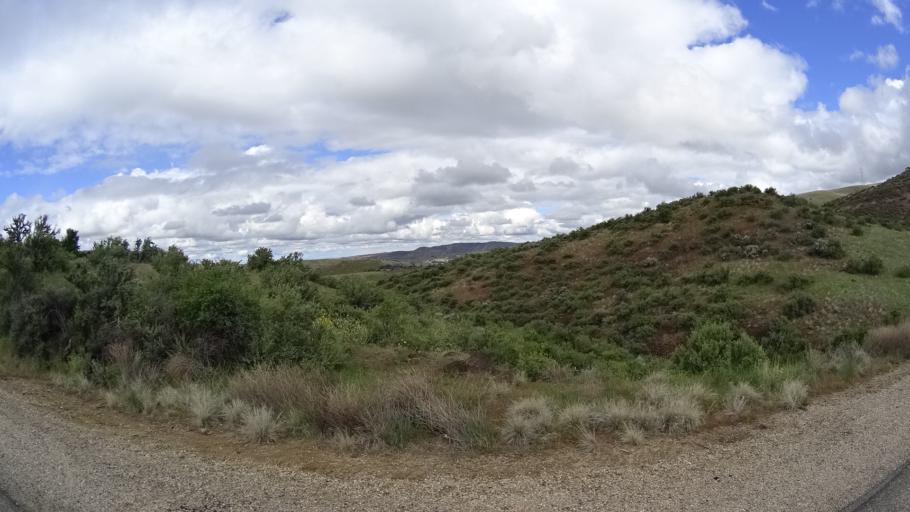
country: US
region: Idaho
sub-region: Ada County
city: Garden City
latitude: 43.7265
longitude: -116.2341
